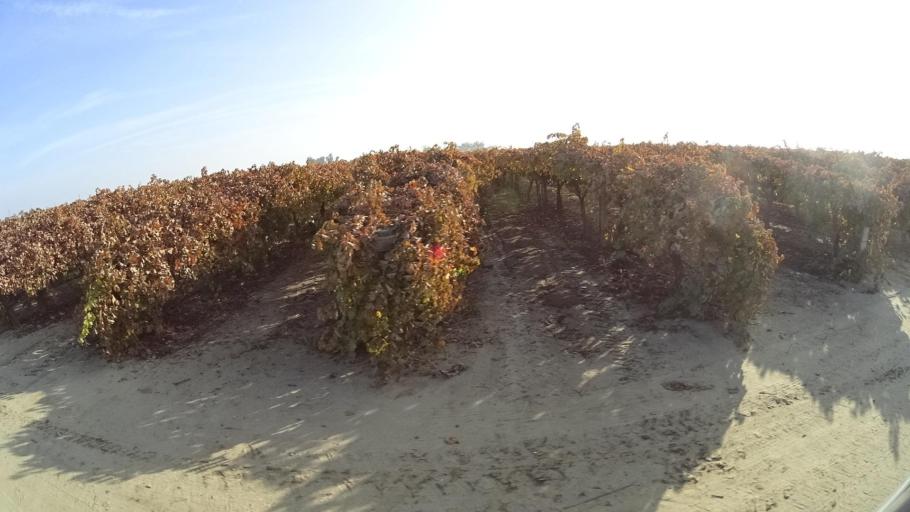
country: US
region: California
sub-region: Kern County
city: Delano
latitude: 35.7441
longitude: -119.1873
